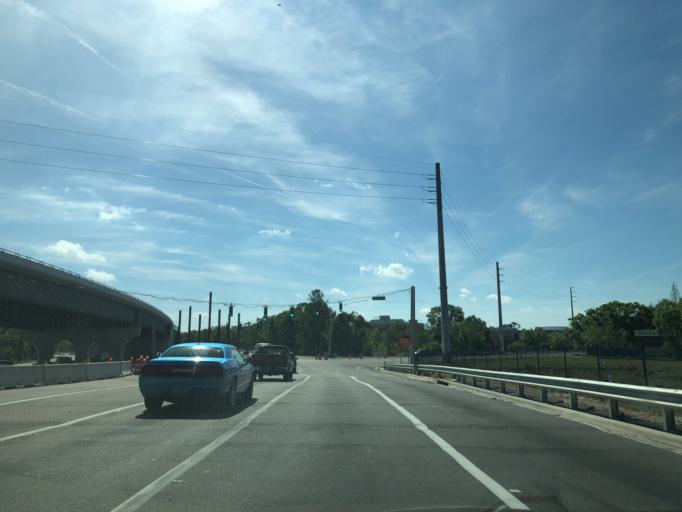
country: US
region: Florida
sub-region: Orange County
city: Eatonville
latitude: 28.6325
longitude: -81.3993
